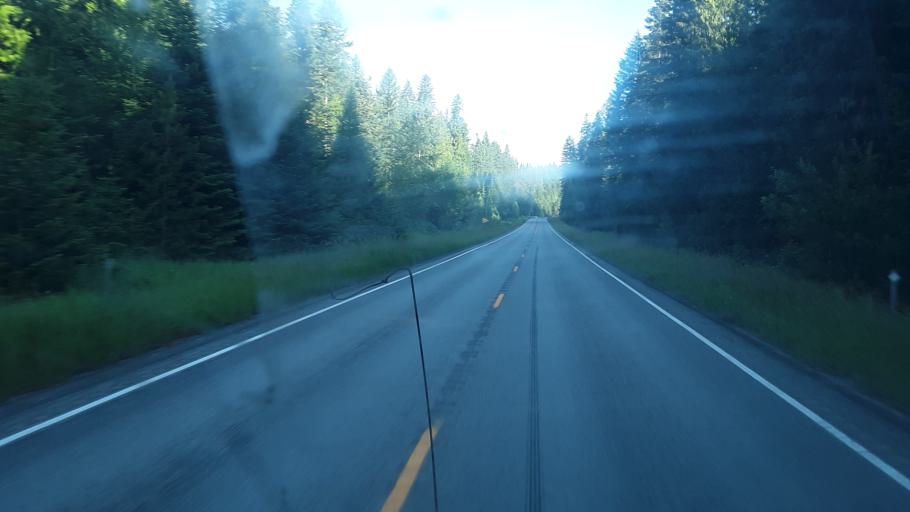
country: US
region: Idaho
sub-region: Boundary County
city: Bonners Ferry
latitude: 48.6087
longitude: -116.0211
